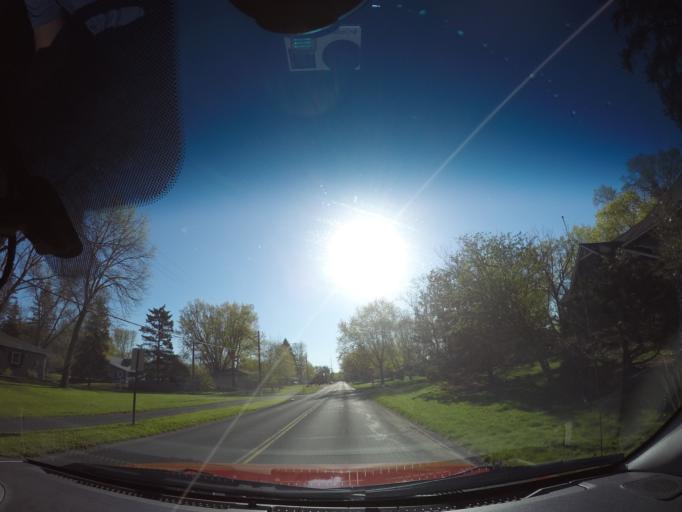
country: US
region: Minnesota
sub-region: Hennepin County
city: Saint Louis Park
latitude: 44.9763
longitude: -93.3505
